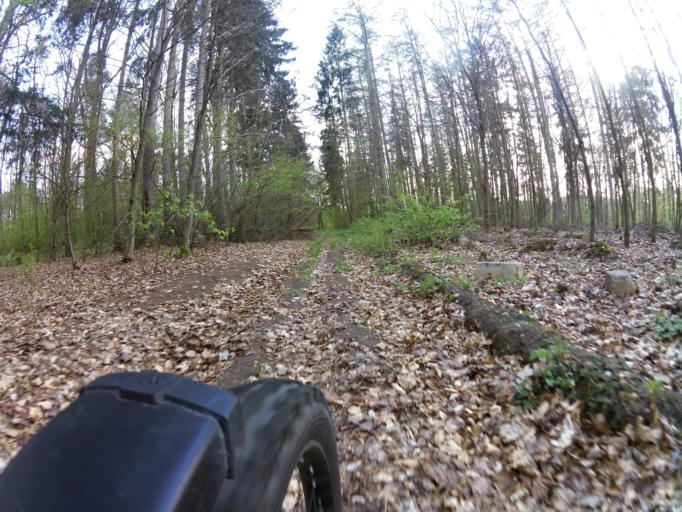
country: PL
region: West Pomeranian Voivodeship
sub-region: Powiat gryficki
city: Ploty
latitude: 53.7781
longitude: 15.2524
